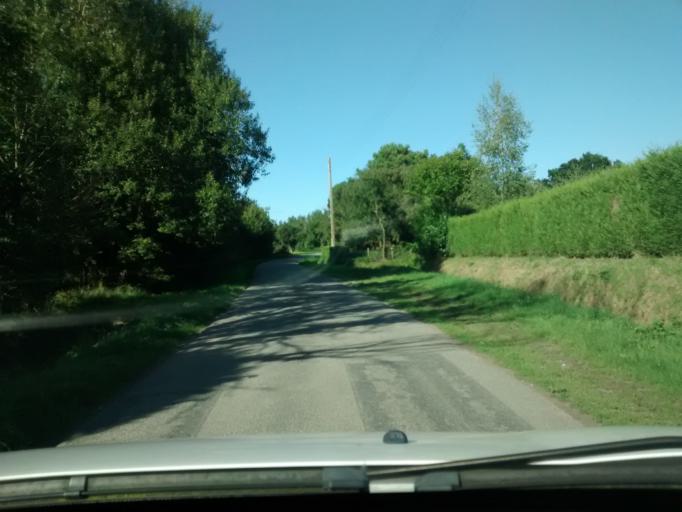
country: FR
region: Brittany
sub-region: Departement d'Ille-et-Vilaine
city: Nouvoitou
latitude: 48.0748
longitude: -1.5633
